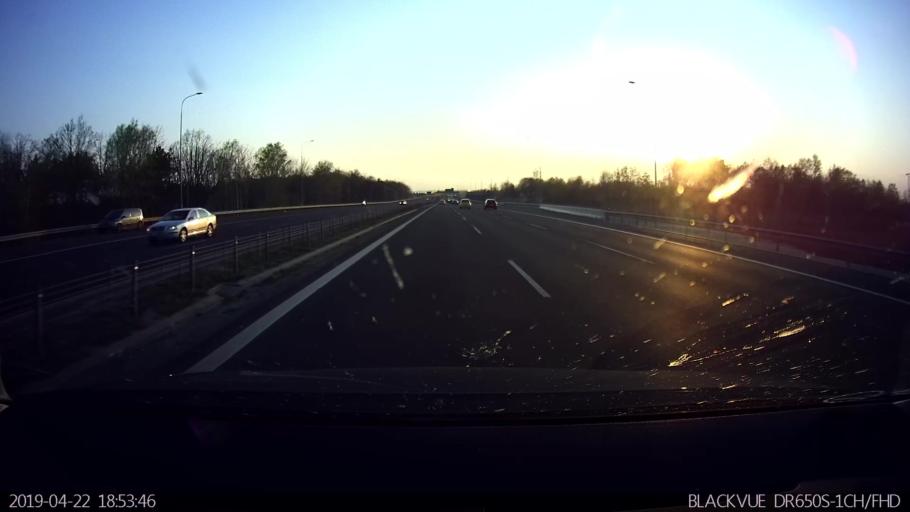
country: PL
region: Masovian Voivodeship
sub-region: Powiat wolominski
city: Marki
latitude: 52.3095
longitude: 21.1164
